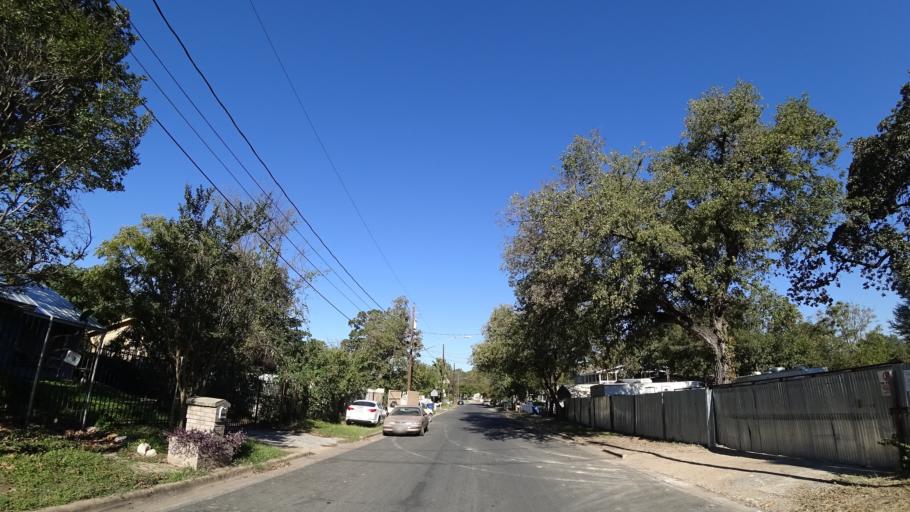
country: US
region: Texas
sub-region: Travis County
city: Austin
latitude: 30.2379
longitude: -97.6916
